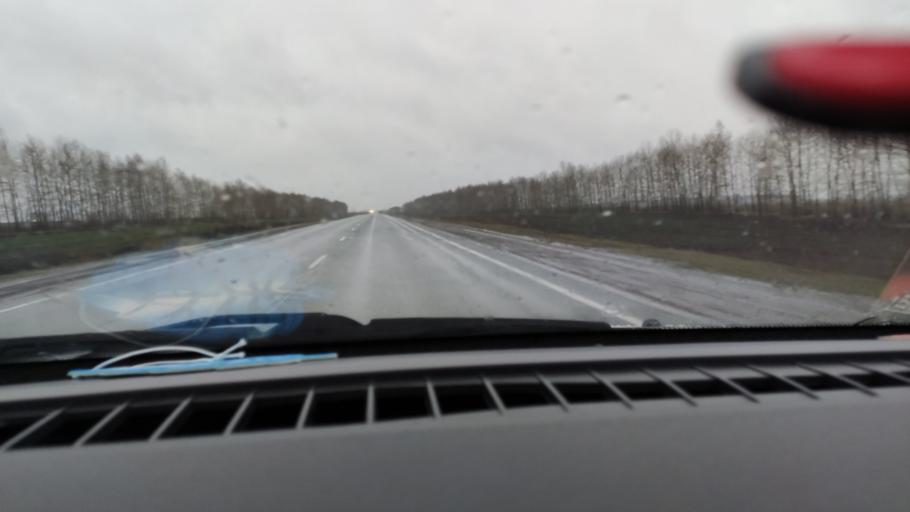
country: RU
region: Tatarstan
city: Mendeleyevsk
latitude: 55.9318
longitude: 52.2828
